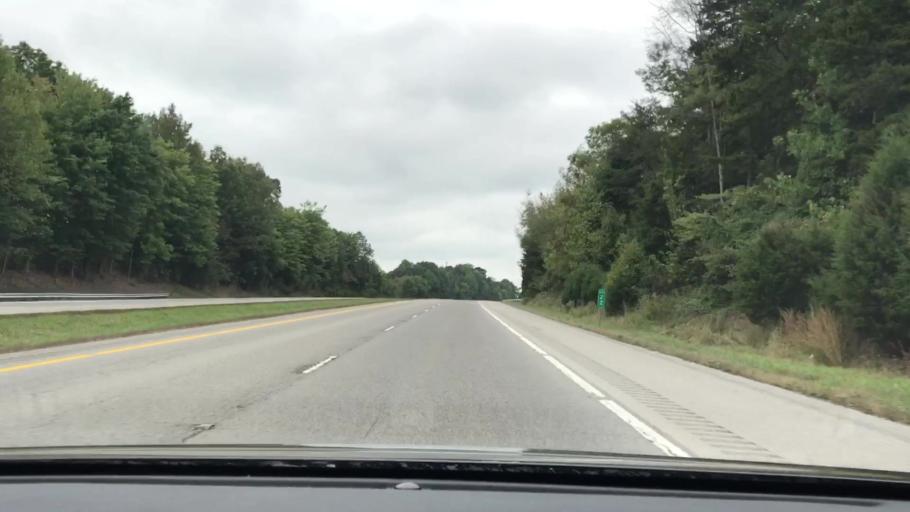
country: US
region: Kentucky
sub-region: Metcalfe County
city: Edmonton
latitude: 36.9954
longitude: -85.7538
